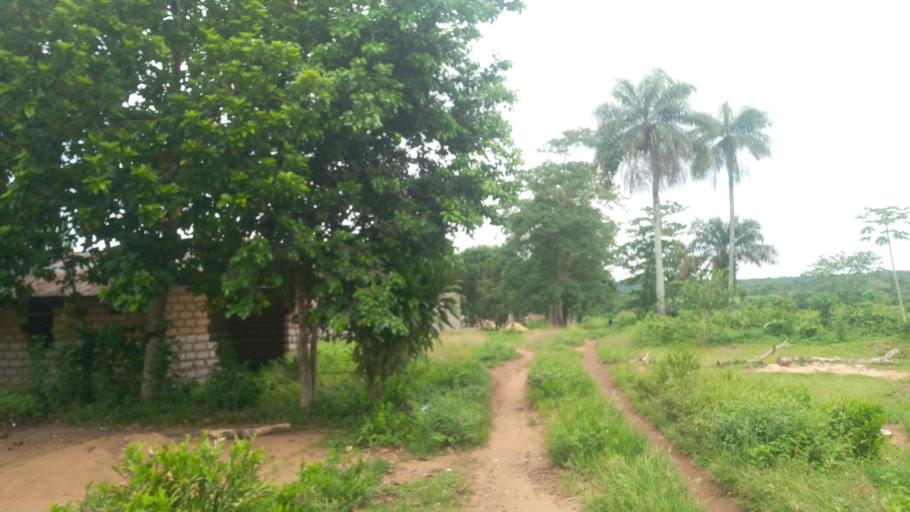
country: SL
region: Southern Province
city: Mogbwemo
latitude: 7.5999
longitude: -12.1770
